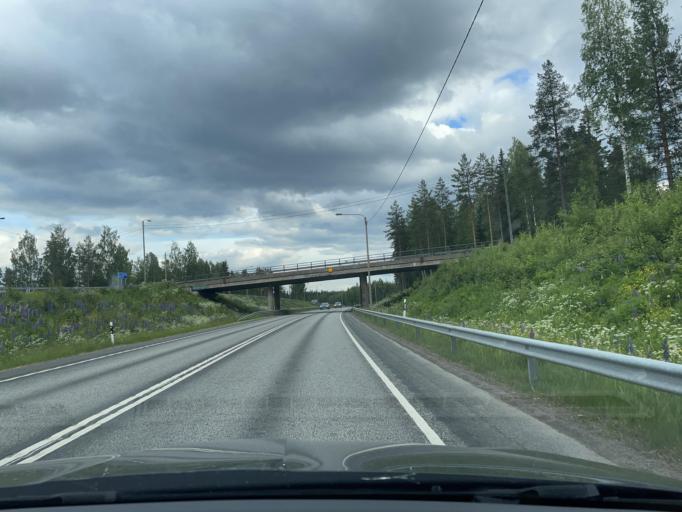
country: FI
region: Central Finland
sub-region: Jyvaeskylae
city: Jyvaeskylae
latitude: 62.2496
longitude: 25.6477
